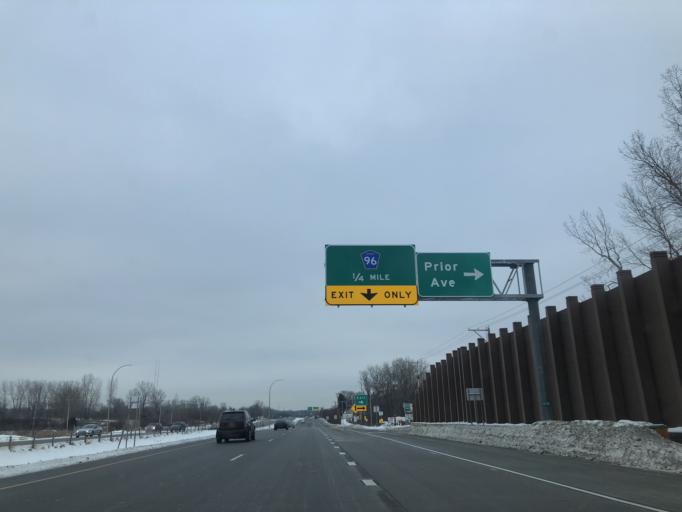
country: US
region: Minnesota
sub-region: Ramsey County
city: New Brighton
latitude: 45.0849
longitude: -93.1832
